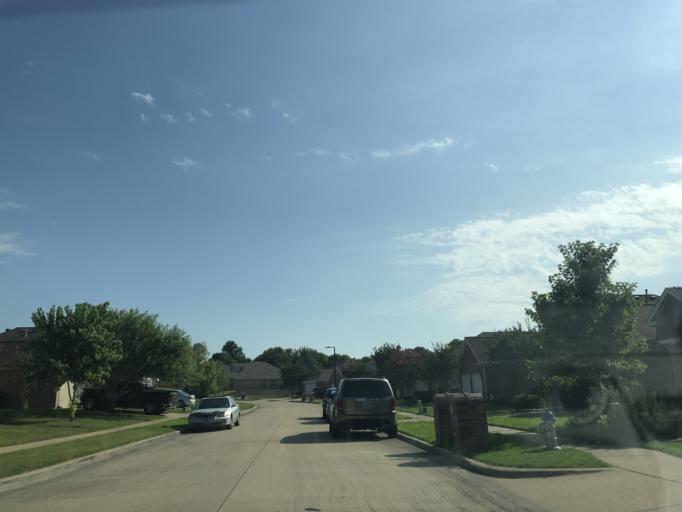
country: US
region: Texas
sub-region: Dallas County
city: Sunnyvale
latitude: 32.8421
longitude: -96.5733
